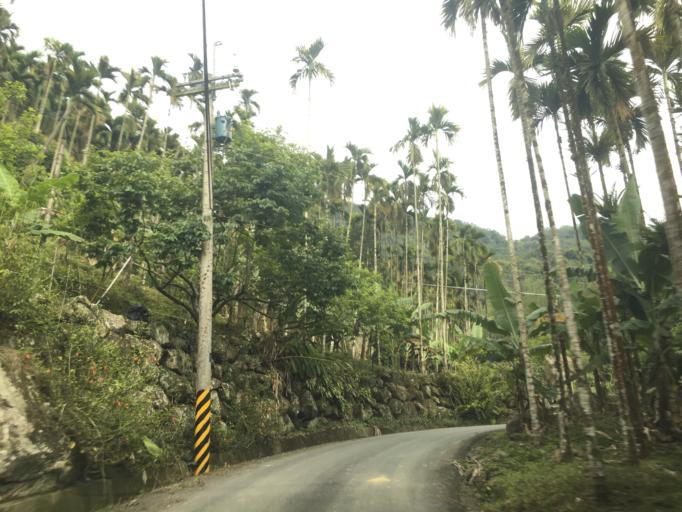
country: TW
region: Taiwan
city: Zhongxing New Village
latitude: 23.9780
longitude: 120.8203
